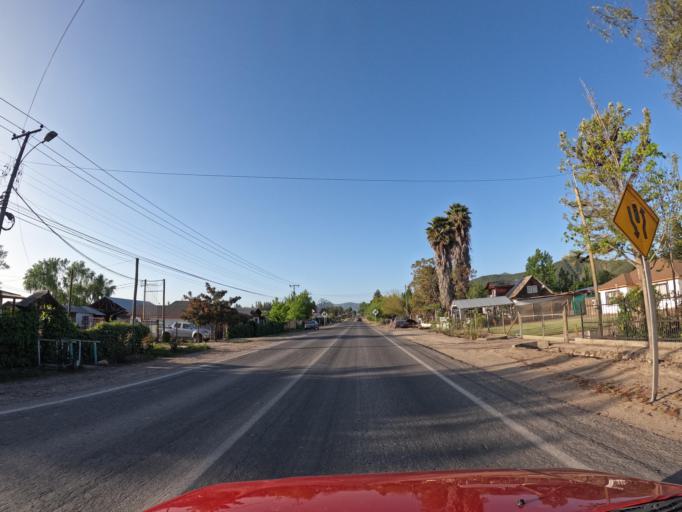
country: CL
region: O'Higgins
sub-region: Provincia de Colchagua
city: Santa Cruz
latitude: -34.4196
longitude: -71.3736
